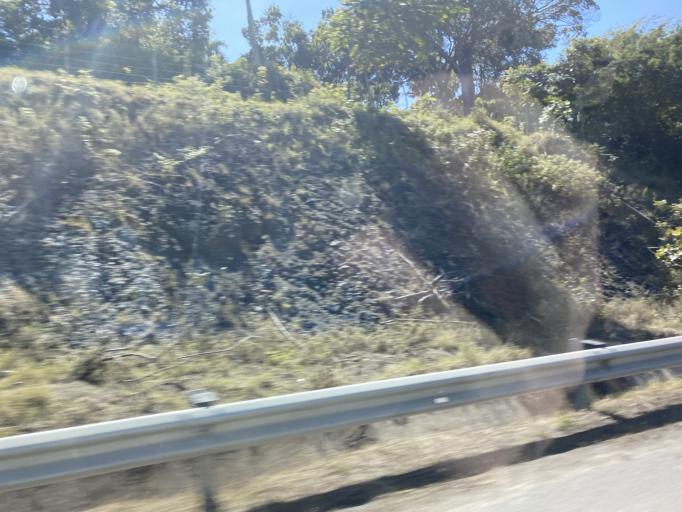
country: DO
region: Puerto Plata
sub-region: Puerto Plata
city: Puerto Plata
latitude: 19.8303
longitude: -70.7677
